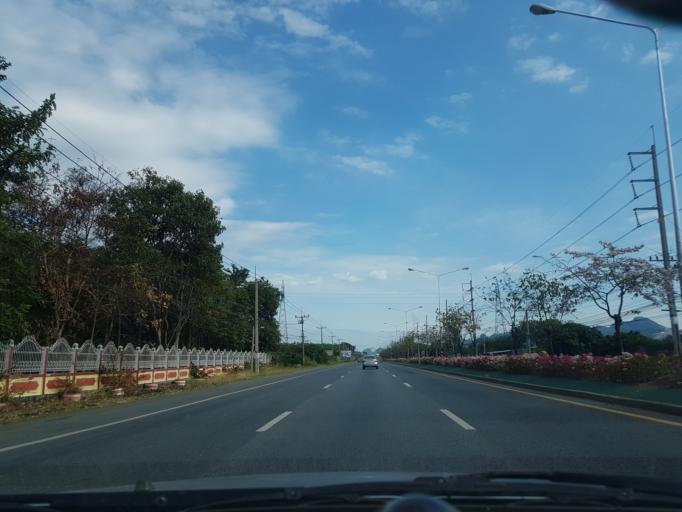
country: TH
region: Sara Buri
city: Phra Phutthabat
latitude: 14.7405
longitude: 100.7659
